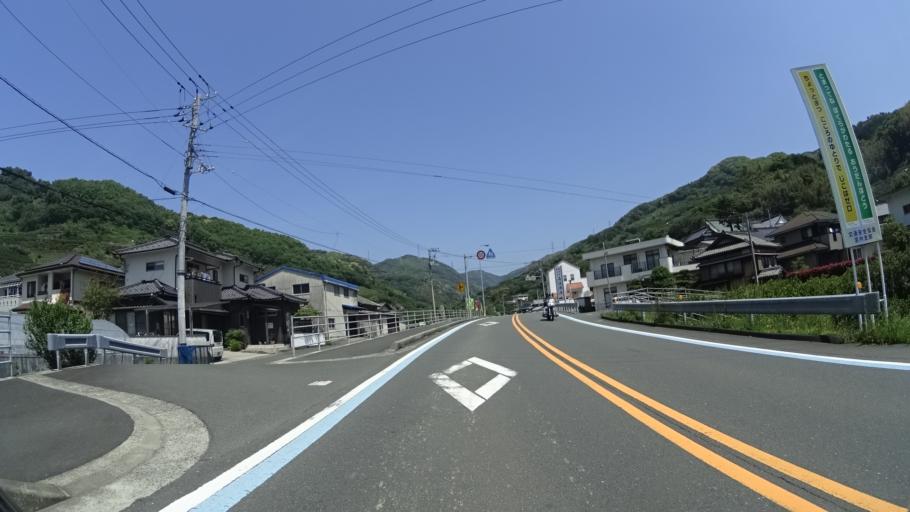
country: JP
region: Ehime
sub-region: Nishiuwa-gun
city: Ikata-cho
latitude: 33.4949
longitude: 132.3970
